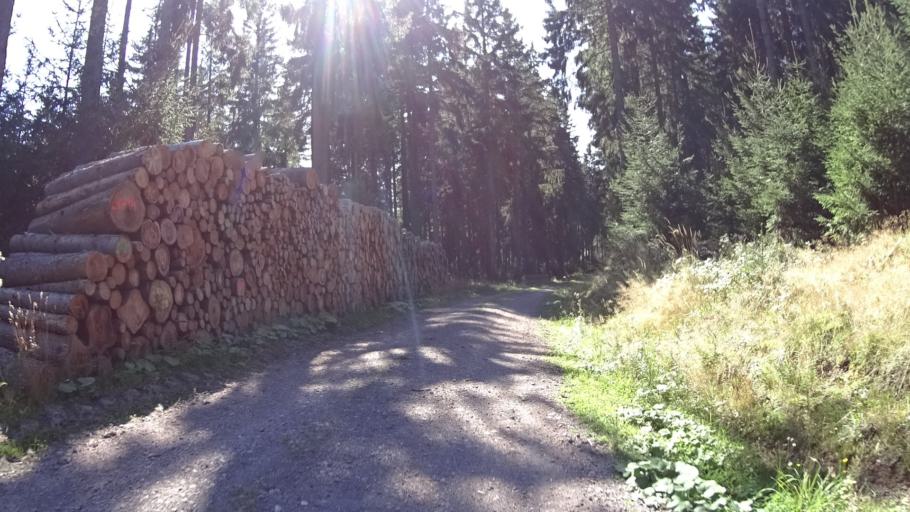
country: DE
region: Thuringia
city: Langewiesen
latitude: 50.6391
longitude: 10.9485
